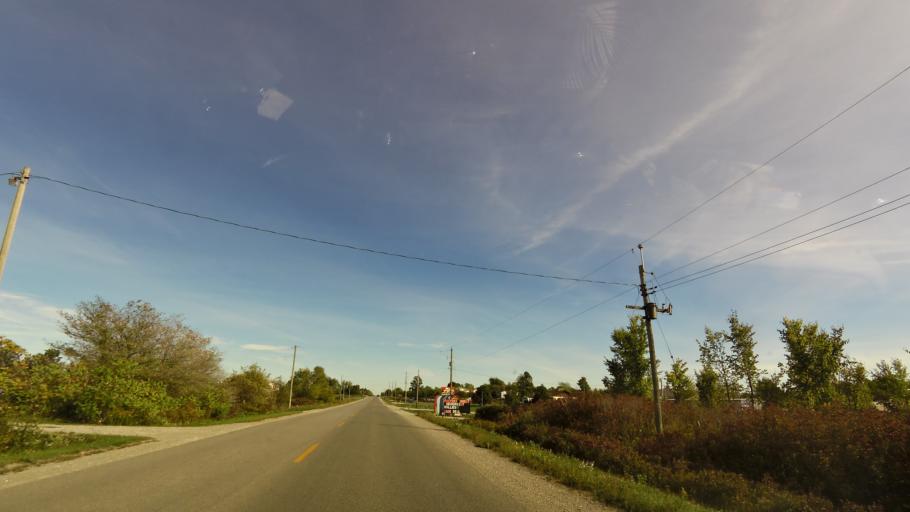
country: CA
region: Ontario
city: Ancaster
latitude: 43.0334
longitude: -80.0220
